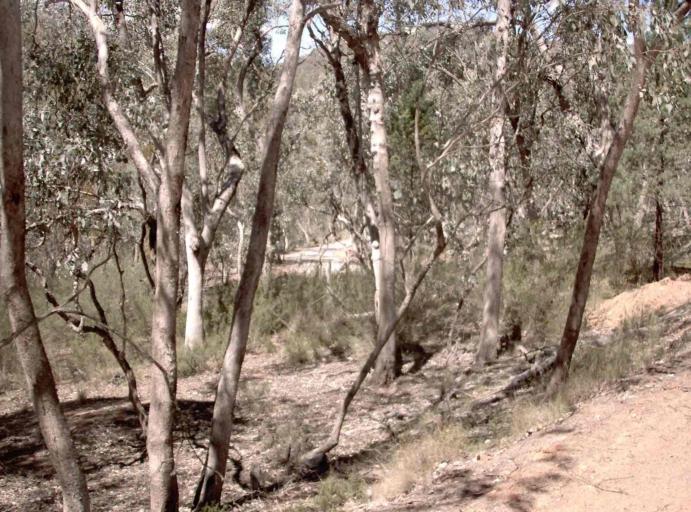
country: AU
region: New South Wales
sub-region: Snowy River
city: Jindabyne
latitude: -37.0635
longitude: 148.5105
